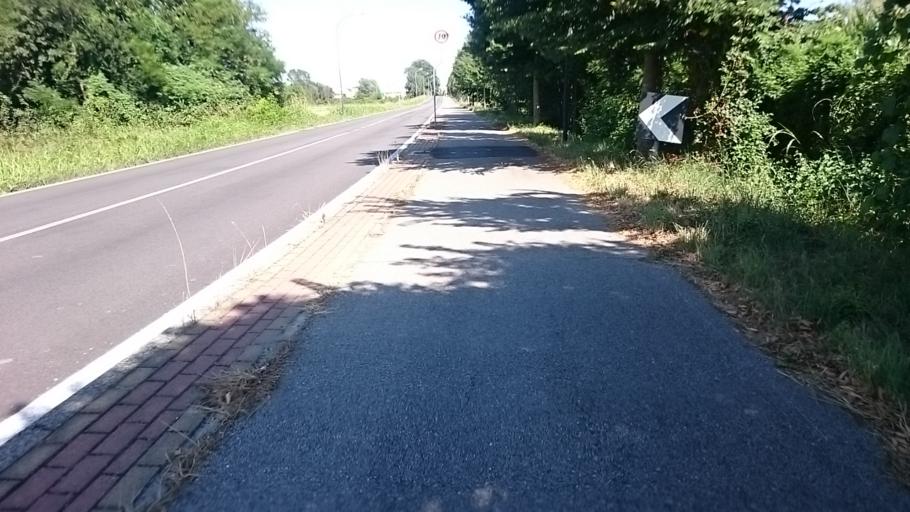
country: IT
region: Veneto
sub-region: Provincia di Venezia
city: Arino
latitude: 45.4273
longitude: 12.0590
